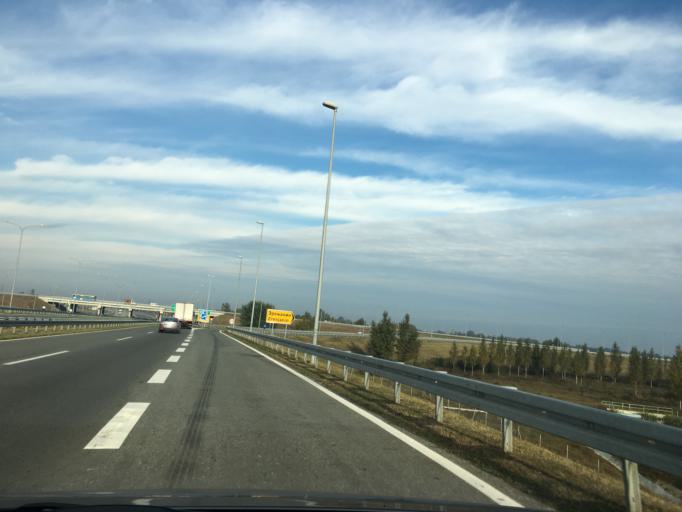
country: RS
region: Autonomna Pokrajina Vojvodina
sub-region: Juznobacki Okrug
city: Petrovaradin
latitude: 45.3021
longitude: 19.8657
